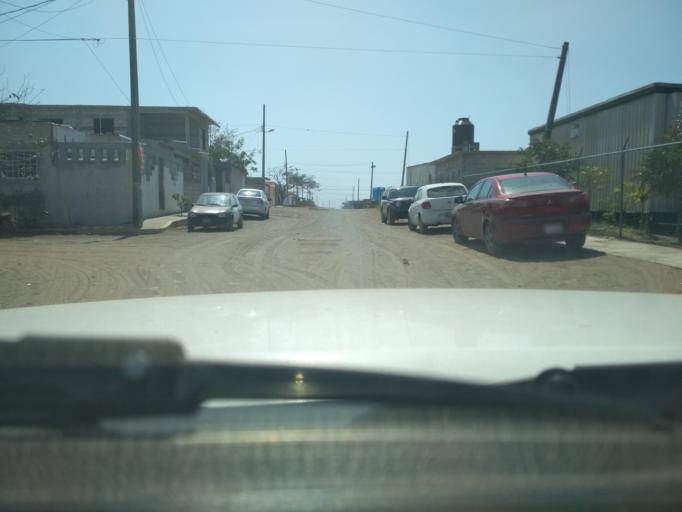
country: MX
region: Veracruz
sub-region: Veracruz
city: Lomas de Rio Medio Cuatro
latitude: 19.1931
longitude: -96.1969
